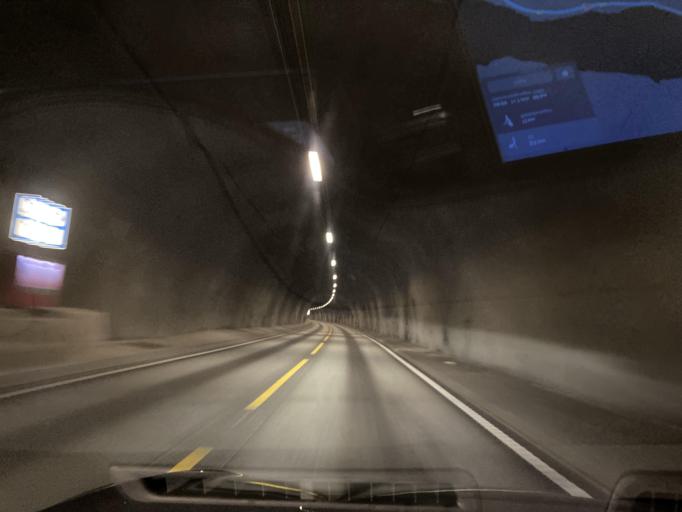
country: NO
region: Rogaland
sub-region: Sauda
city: Sauda
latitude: 59.8305
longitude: 6.2651
